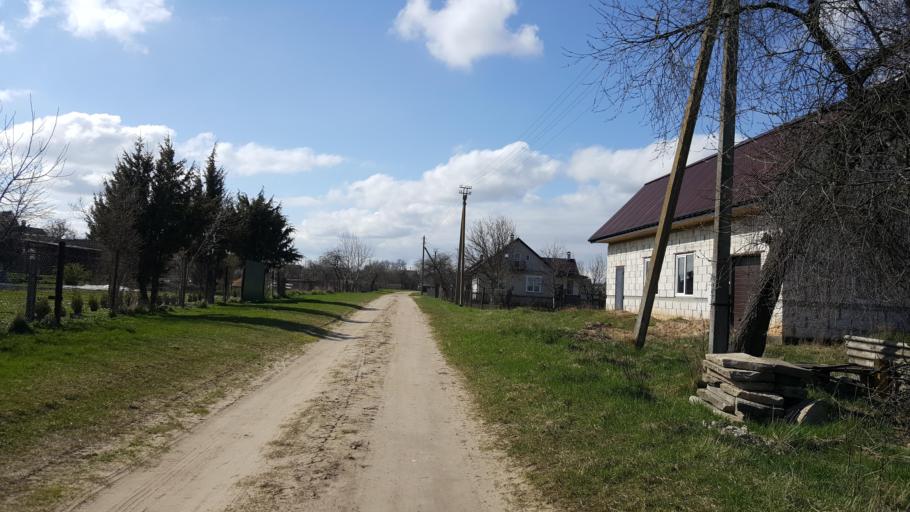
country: BY
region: Brest
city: Kamyanyets
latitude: 52.4044
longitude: 23.8014
